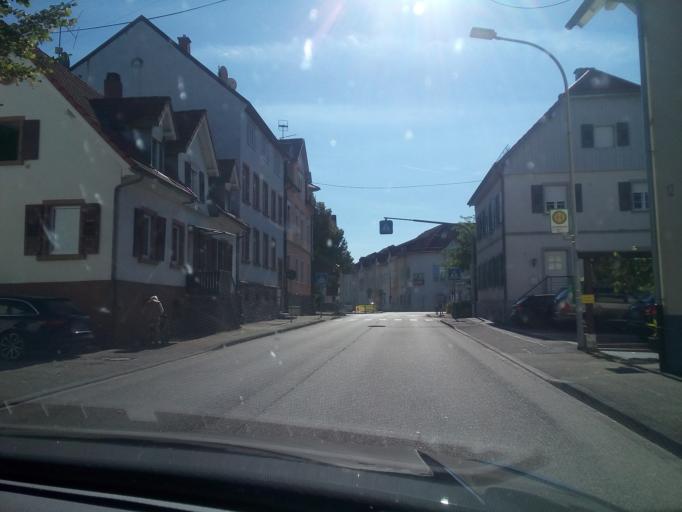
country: DE
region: Baden-Wuerttemberg
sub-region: Freiburg Region
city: Oberkirch
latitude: 48.5334
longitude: 8.0775
